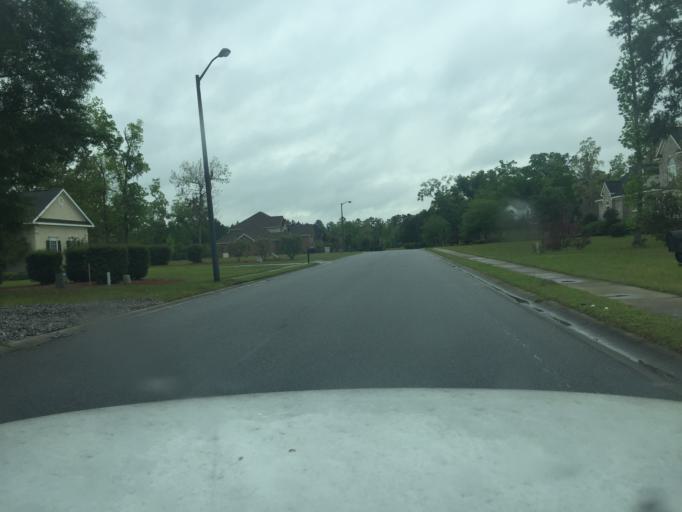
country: US
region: Georgia
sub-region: Chatham County
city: Pooler
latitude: 32.0524
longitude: -81.2412
